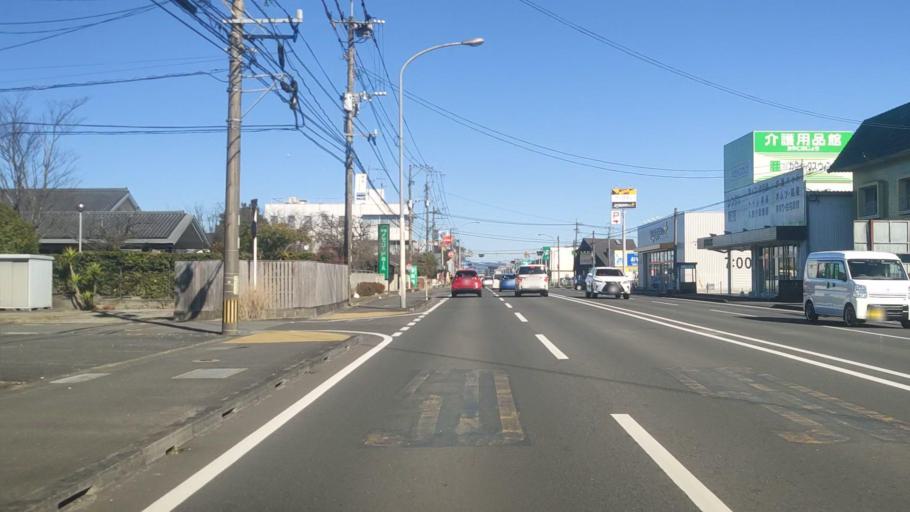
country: JP
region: Miyazaki
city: Miyakonojo
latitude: 31.7429
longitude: 131.0742
